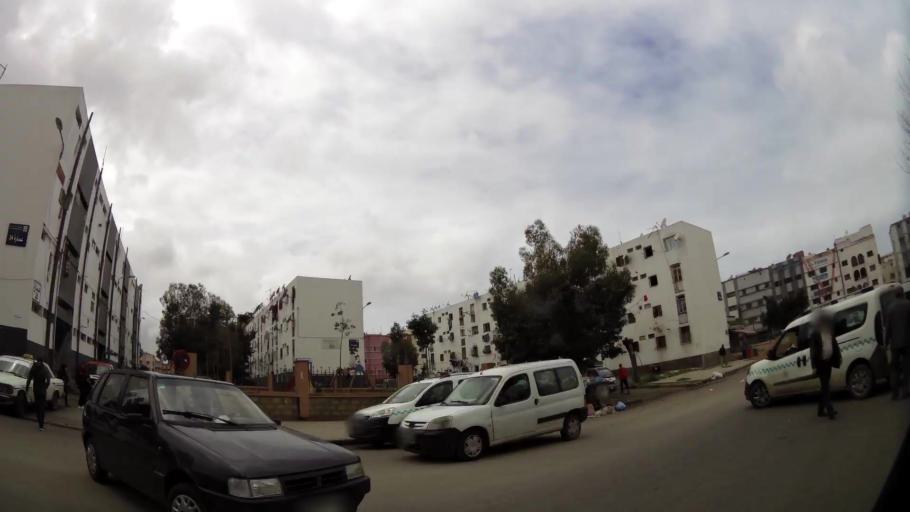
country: MA
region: Grand Casablanca
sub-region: Mediouna
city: Tit Mellil
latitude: 33.6071
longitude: -7.5152
